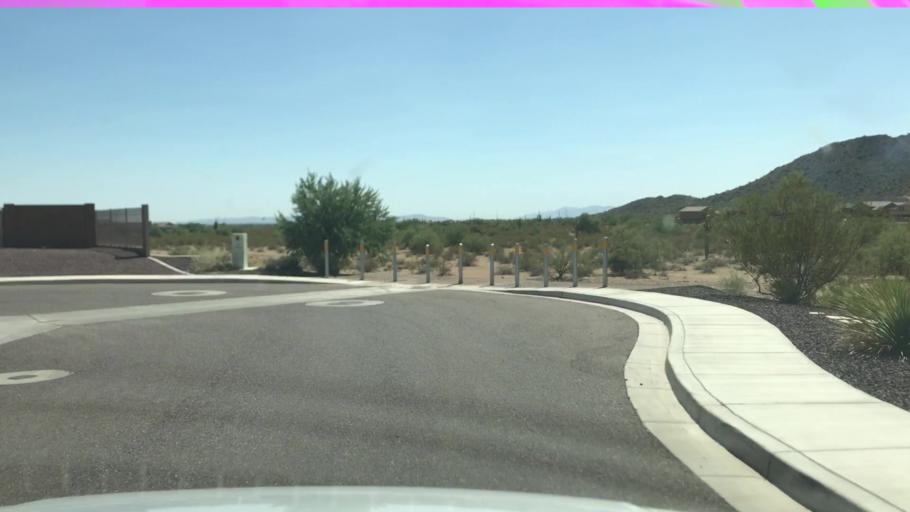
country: US
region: Arizona
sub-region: Maricopa County
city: Sun City West
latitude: 33.7299
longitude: -112.2358
